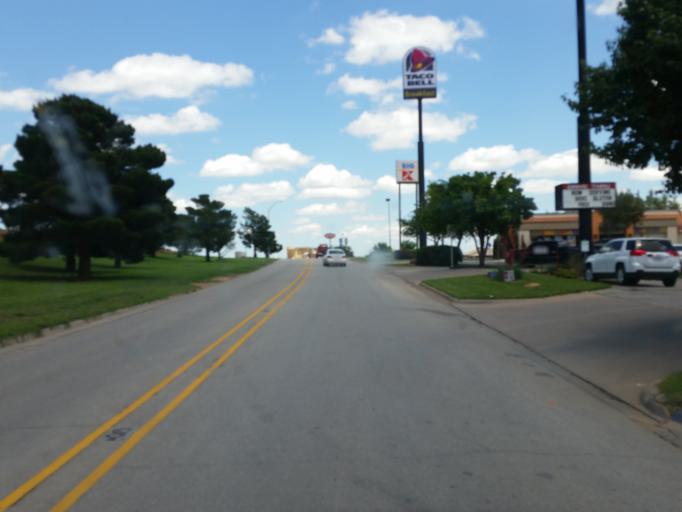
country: US
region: Texas
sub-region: Nolan County
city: Sweetwater
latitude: 32.4498
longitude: -100.3978
